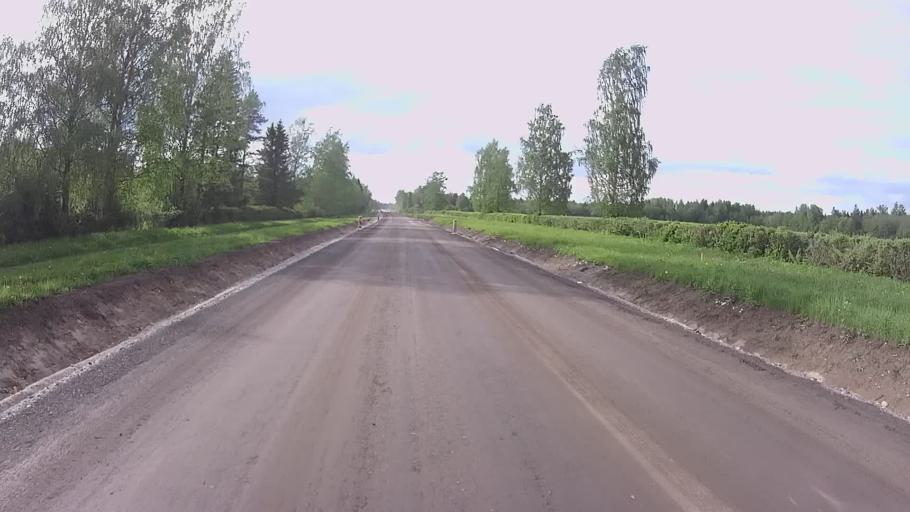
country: EE
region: Jogevamaa
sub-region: Mustvee linn
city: Mustvee
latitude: 59.0228
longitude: 26.6994
